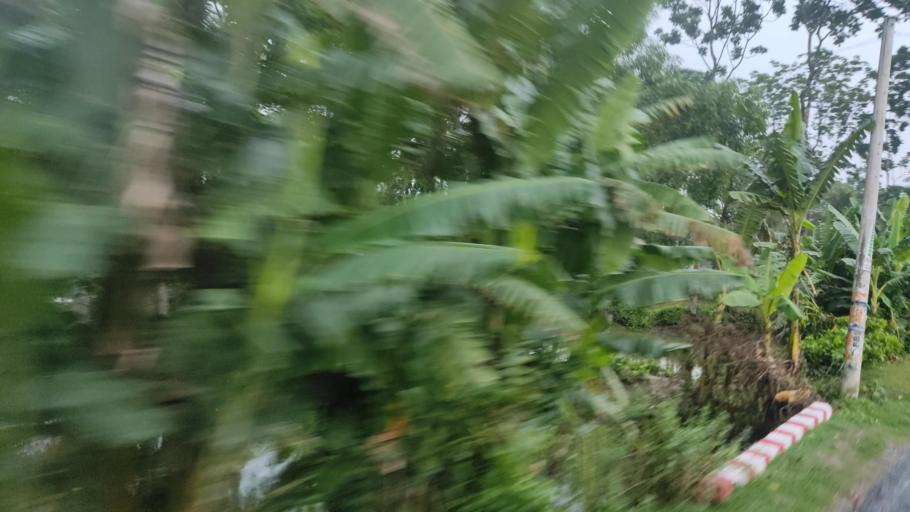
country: BD
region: Barisal
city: Bhandaria
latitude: 22.3074
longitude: 90.3247
